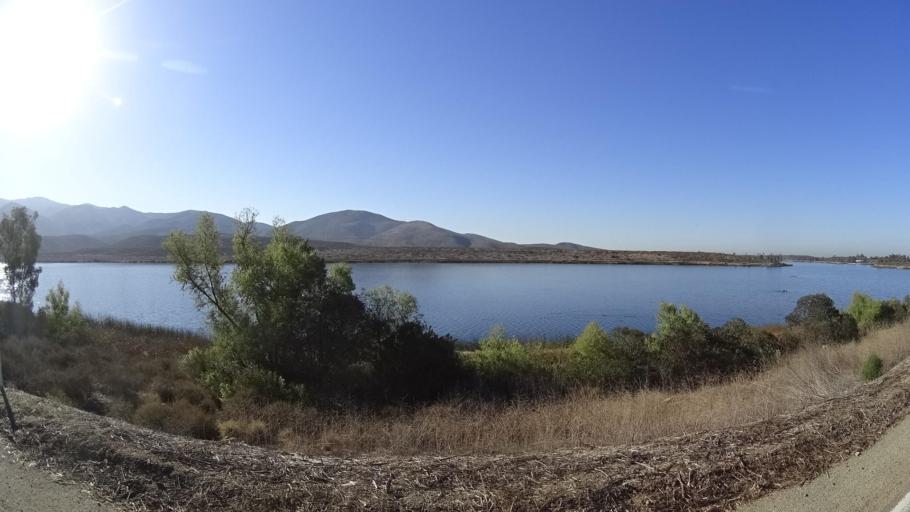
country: US
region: California
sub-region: San Diego County
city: Jamul
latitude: 32.6340
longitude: -116.9161
